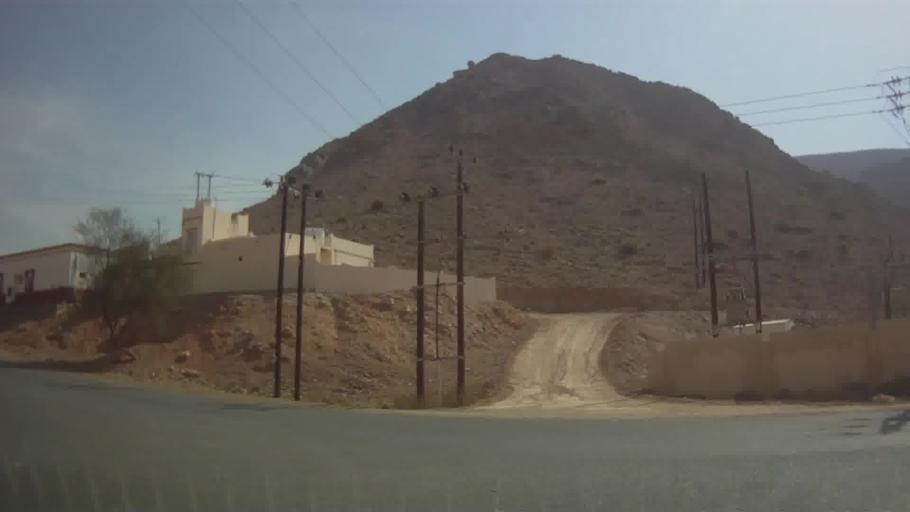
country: OM
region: Muhafazat Masqat
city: Muscat
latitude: 23.5044
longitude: 58.7320
